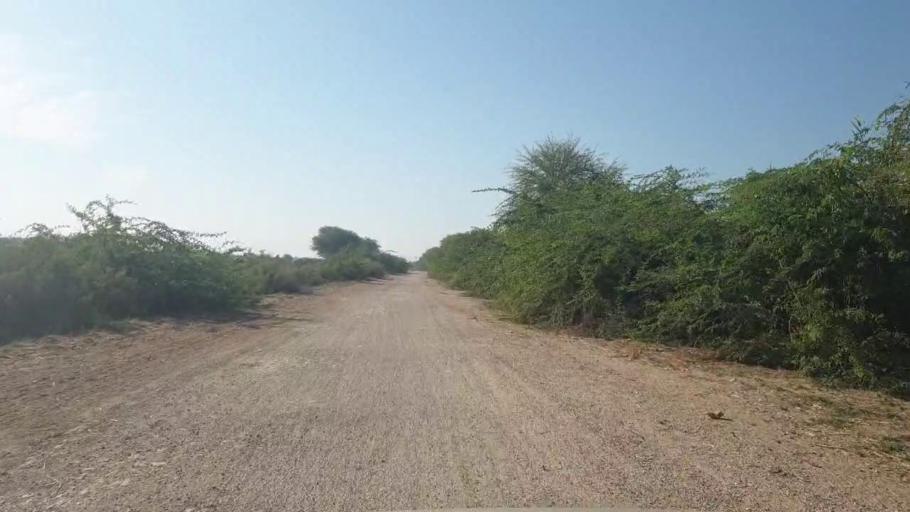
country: PK
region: Sindh
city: Rajo Khanani
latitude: 24.9560
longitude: 68.7956
